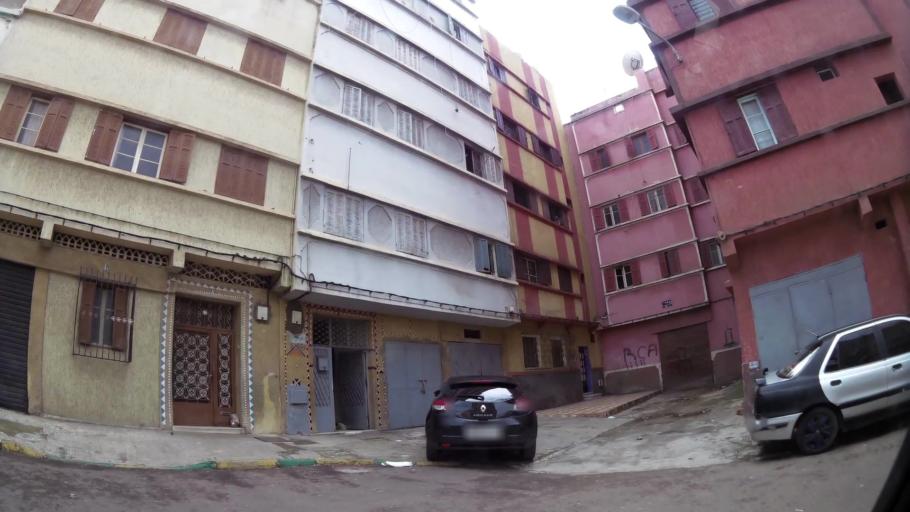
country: MA
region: Grand Casablanca
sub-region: Mediouna
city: Tit Mellil
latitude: 33.6060
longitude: -7.5173
